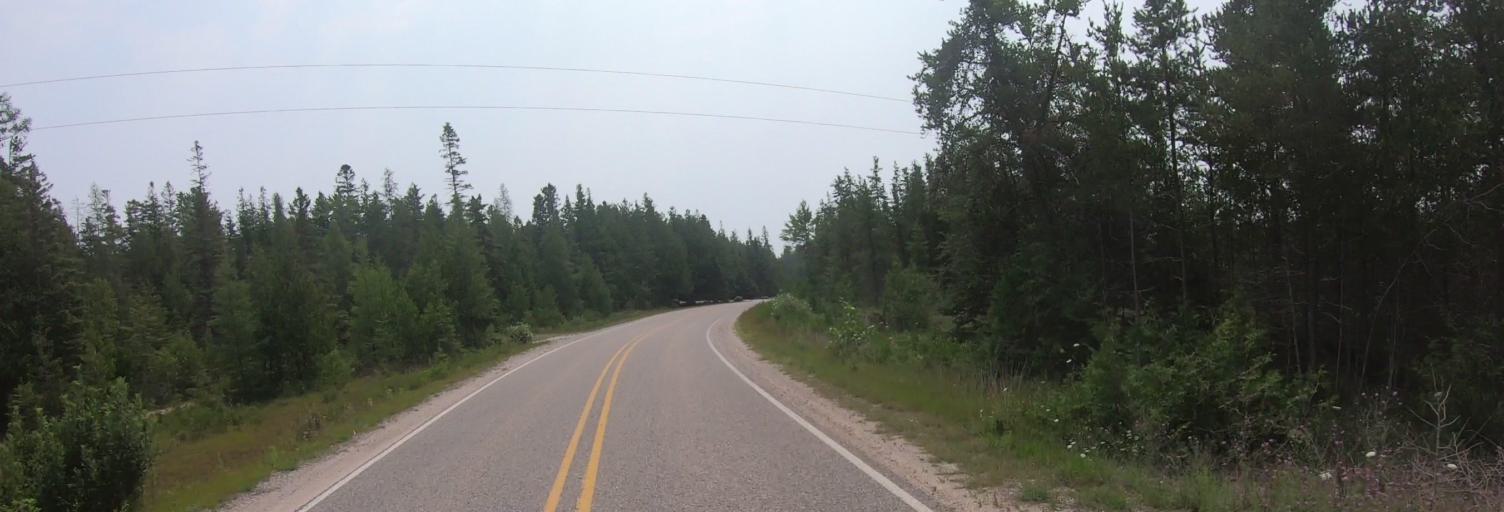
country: CA
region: Ontario
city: Thessalon
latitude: 45.9585
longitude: -83.6258
